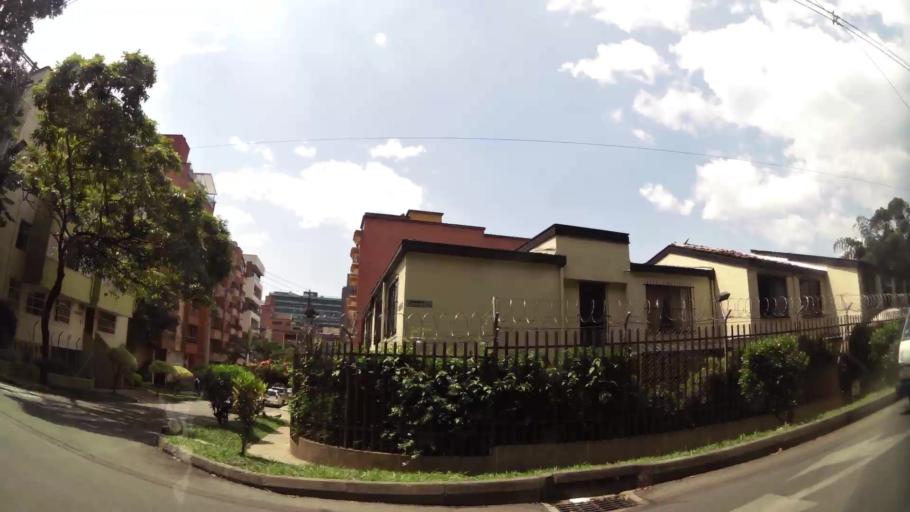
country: CO
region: Antioquia
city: Envigado
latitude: 6.1754
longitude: -75.5884
